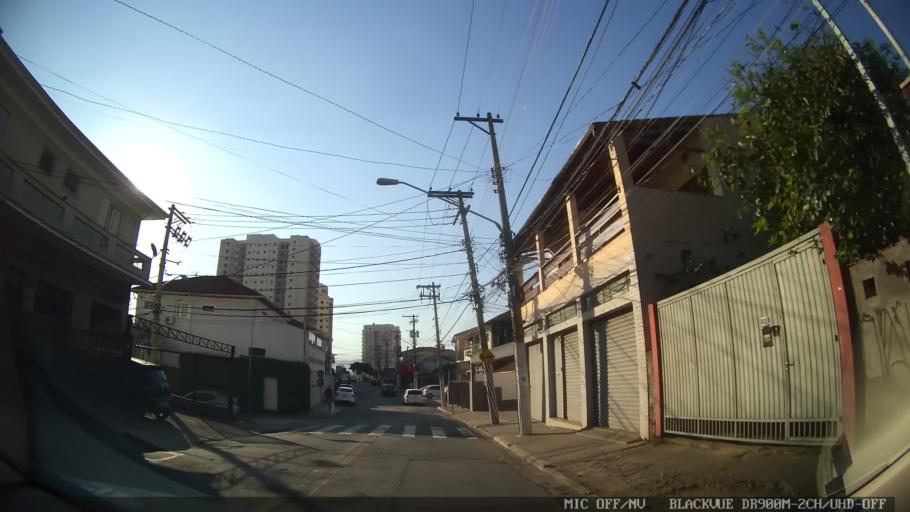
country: BR
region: Sao Paulo
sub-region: Sao Paulo
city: Sao Paulo
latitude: -23.4911
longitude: -46.6420
